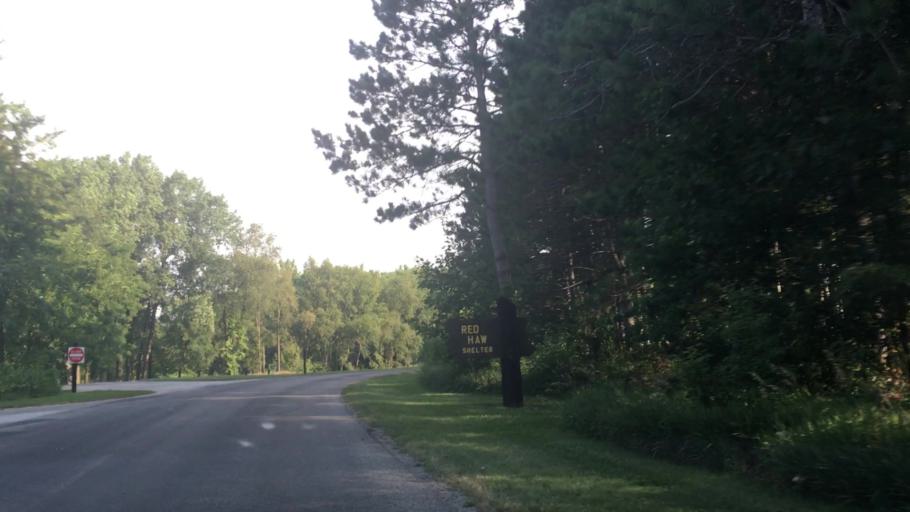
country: US
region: Iowa
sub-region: Johnson County
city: Tiffin
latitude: 41.7299
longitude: -91.7246
